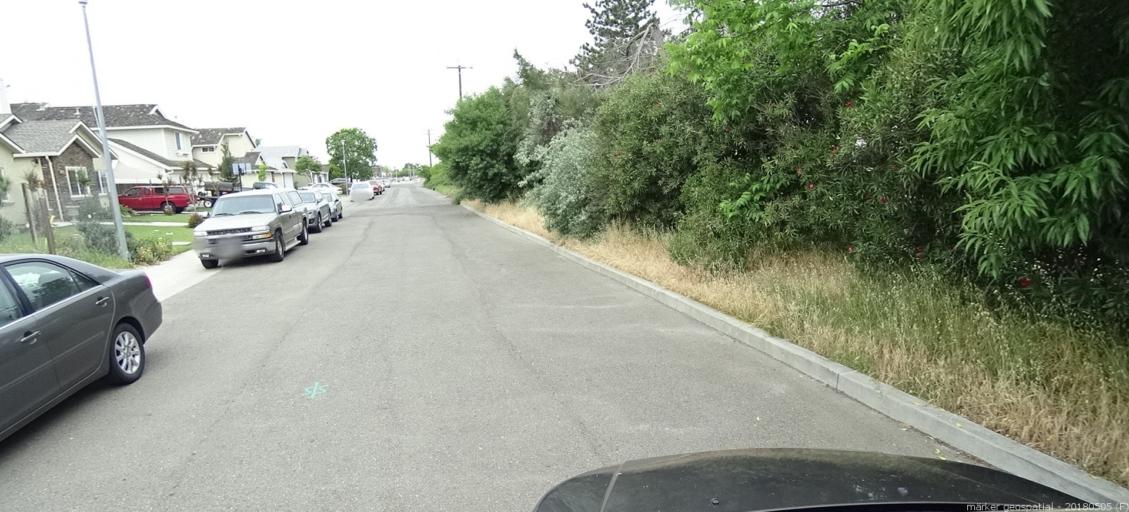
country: US
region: California
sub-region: Sacramento County
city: Rio Linda
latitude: 38.6511
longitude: -121.4415
